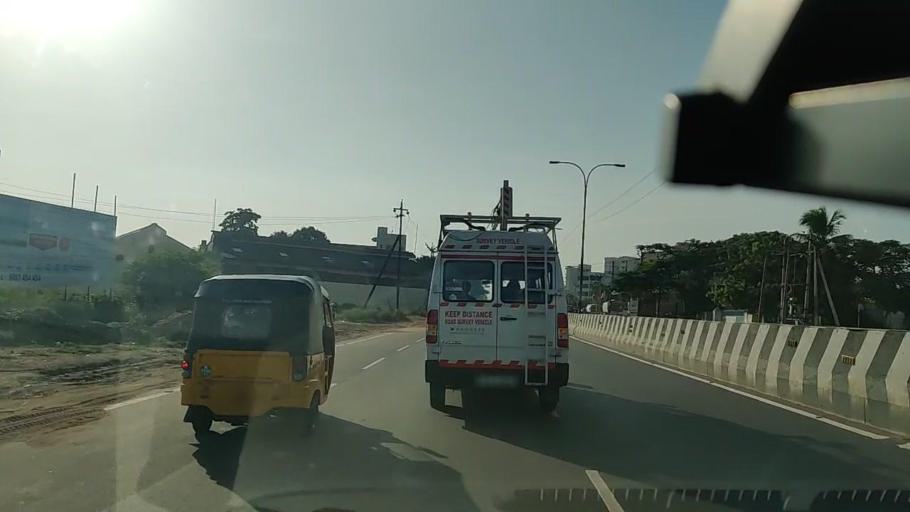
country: IN
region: Tamil Nadu
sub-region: Thiruvallur
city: Chinnasekkadu
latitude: 13.1415
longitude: 80.2245
